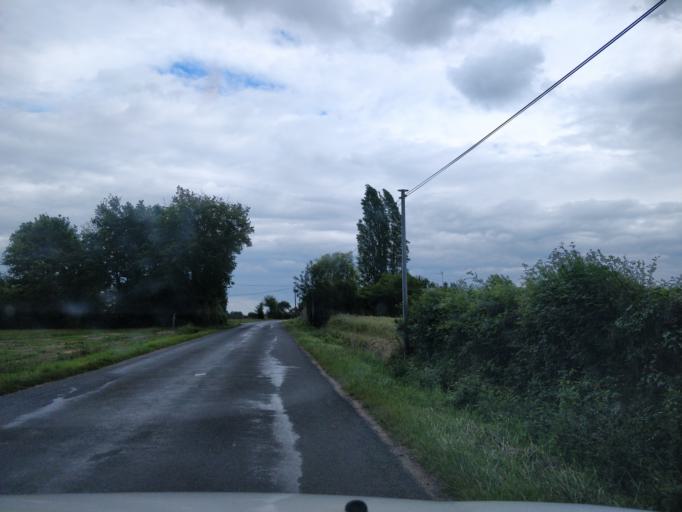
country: FR
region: Pays de la Loire
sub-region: Departement de Maine-et-Loire
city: Grez-Neuville
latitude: 47.6375
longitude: -0.6381
